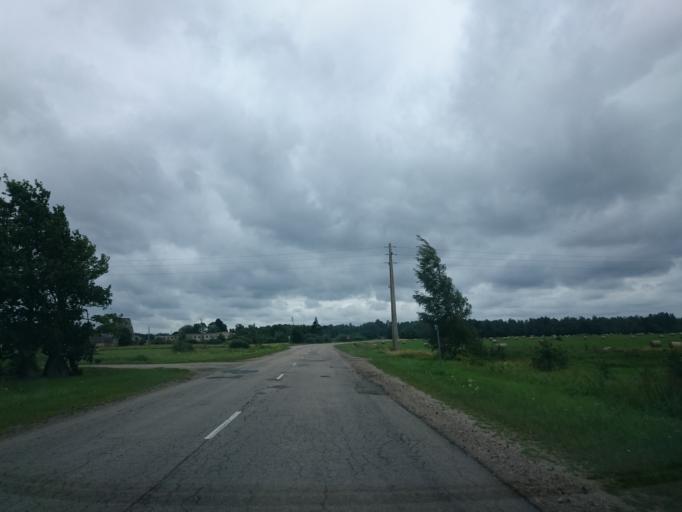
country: LV
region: Pavilostas
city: Pavilosta
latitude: 56.8698
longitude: 21.2249
